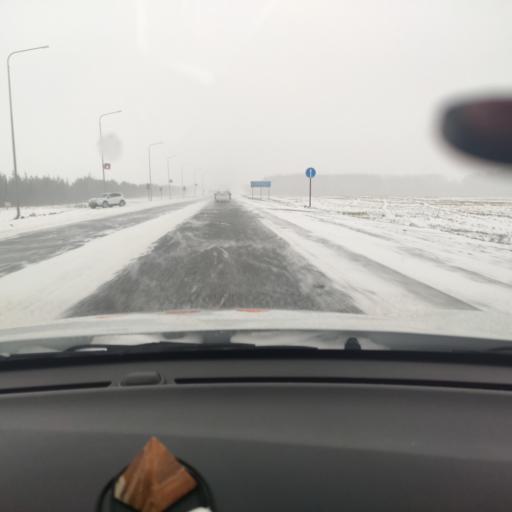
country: RU
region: Tatarstan
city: Verkhniy Uslon
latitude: 55.6604
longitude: 48.8580
